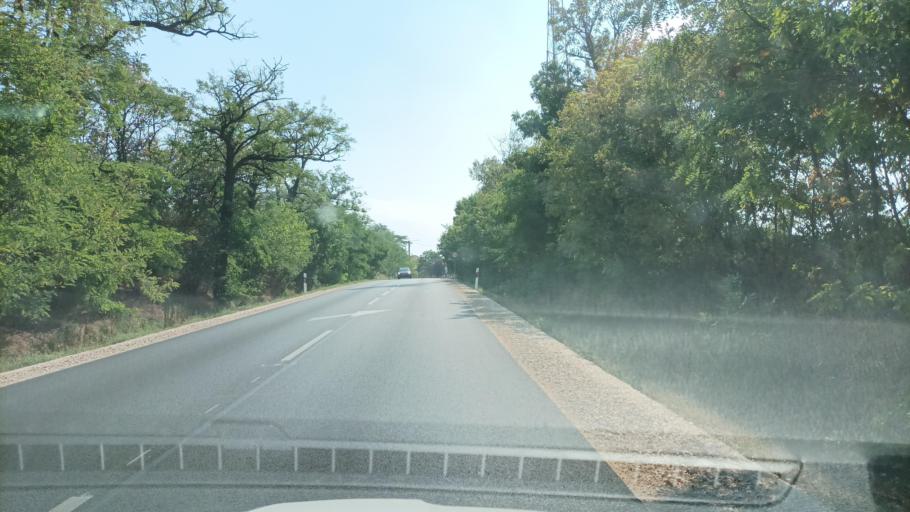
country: HU
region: Pest
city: Gomba
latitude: 47.3666
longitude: 19.5150
